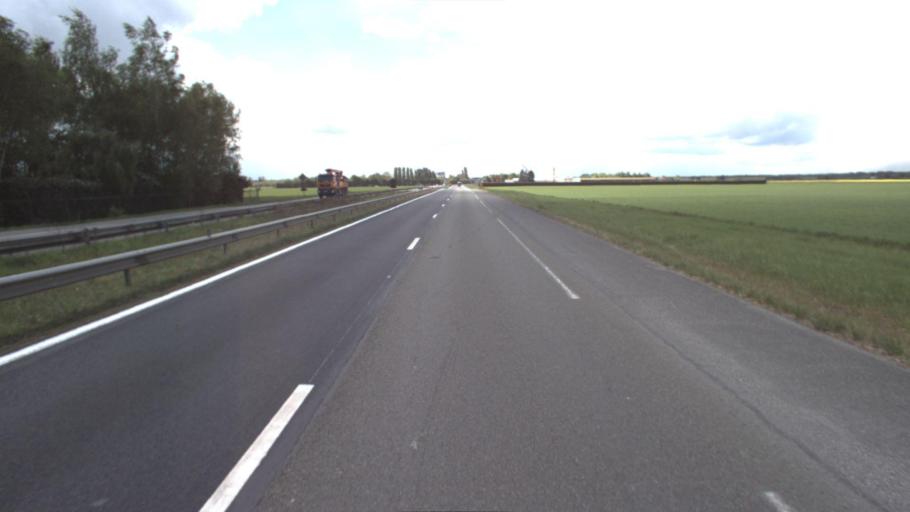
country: FR
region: Ile-de-France
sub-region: Departement de Seine-et-Marne
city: Rozay-en-Brie
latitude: 48.6866
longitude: 2.9776
